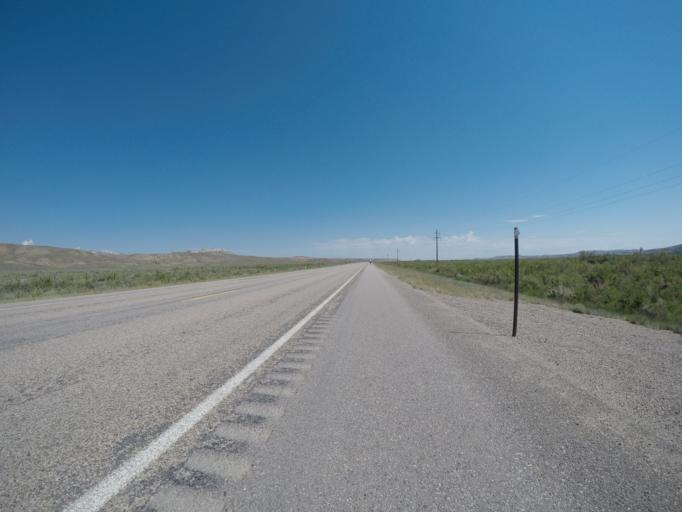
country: US
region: Wyoming
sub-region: Sublette County
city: Marbleton
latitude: 42.3589
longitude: -110.1553
